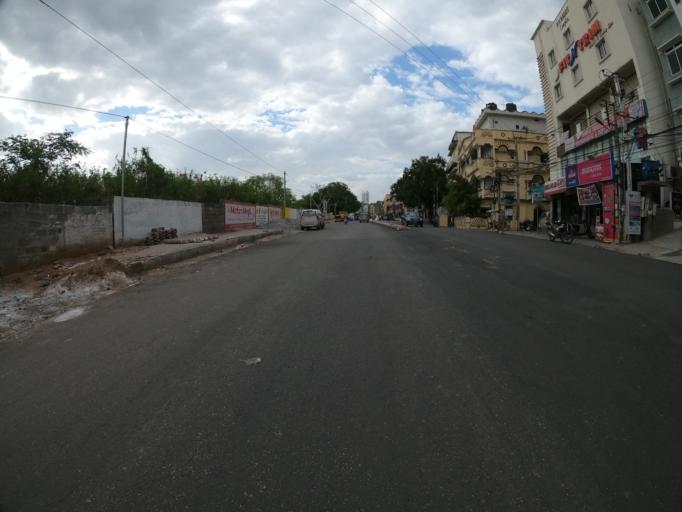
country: IN
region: Telangana
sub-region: Hyderabad
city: Hyderabad
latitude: 17.4109
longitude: 78.3949
